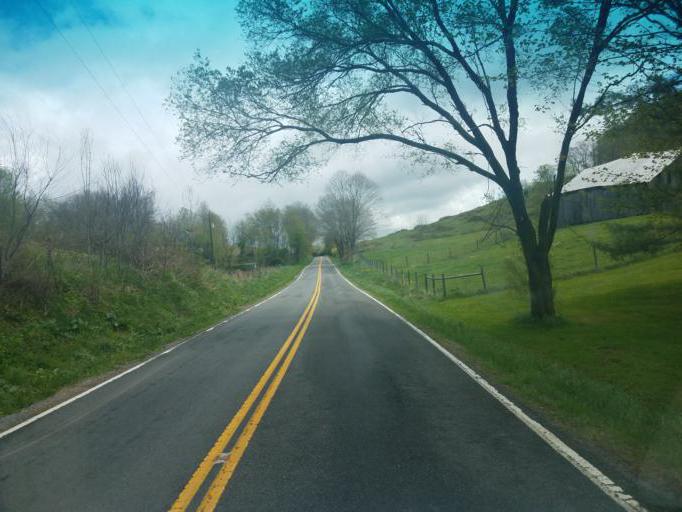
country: US
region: Virginia
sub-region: Smyth County
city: Atkins
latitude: 36.9897
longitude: -81.3860
